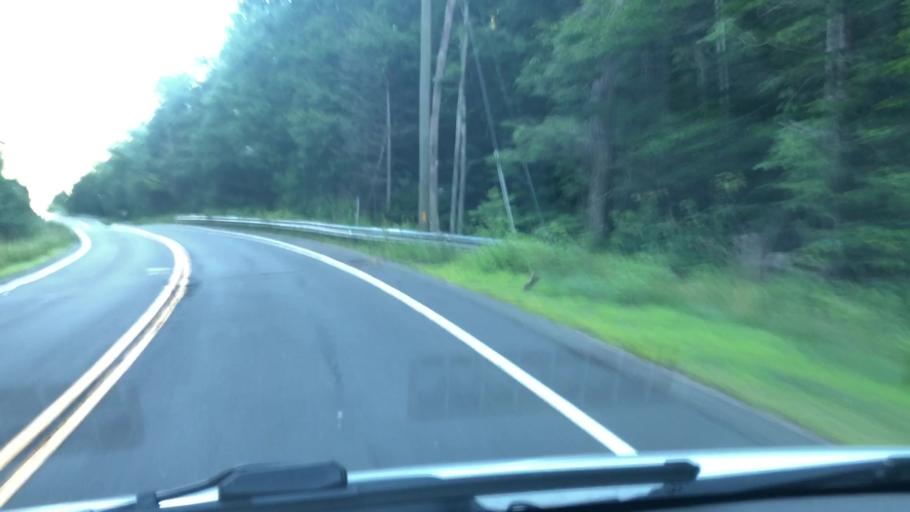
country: US
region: Massachusetts
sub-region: Hampshire County
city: Westhampton
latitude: 42.2846
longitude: -72.8431
